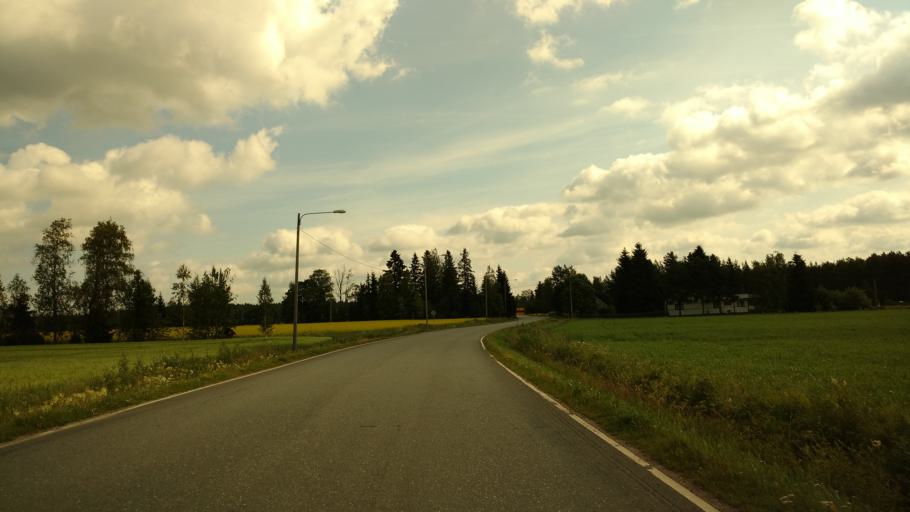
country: FI
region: Varsinais-Suomi
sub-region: Loimaa
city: Koski Tl
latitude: 60.6461
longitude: 23.1194
